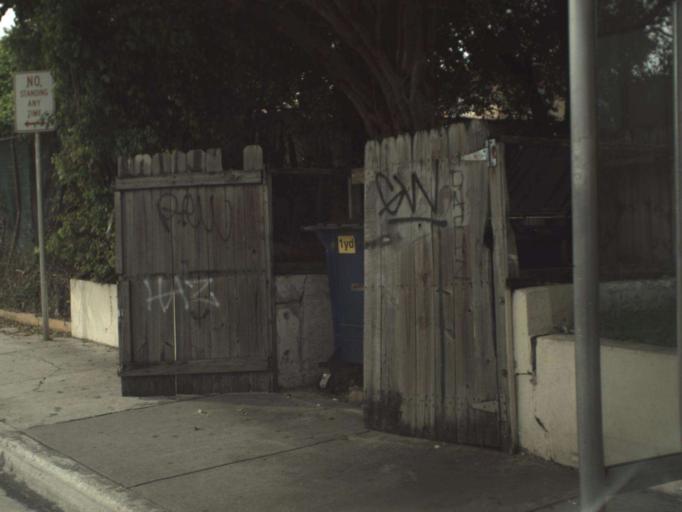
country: US
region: Florida
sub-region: Miami-Dade County
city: Miami
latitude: 25.7670
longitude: -80.2061
